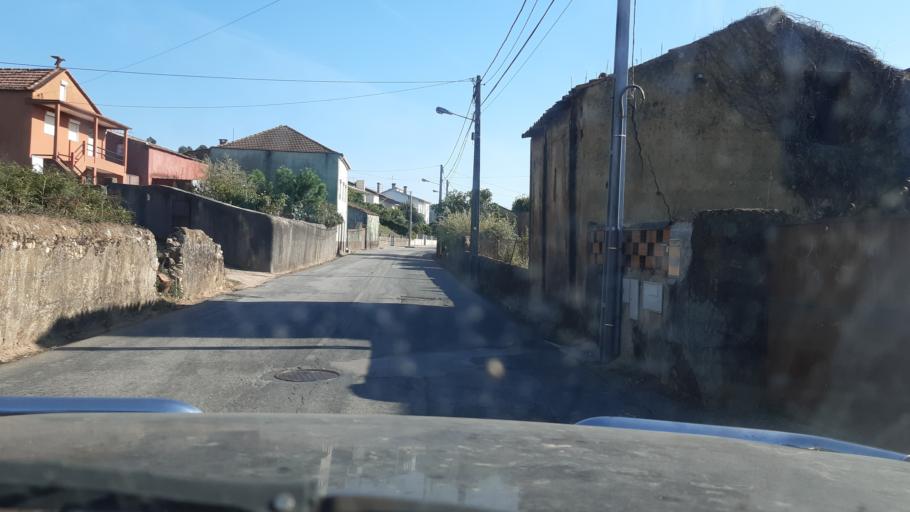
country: PT
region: Aveiro
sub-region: Agueda
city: Agueda
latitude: 40.5686
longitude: -8.4337
